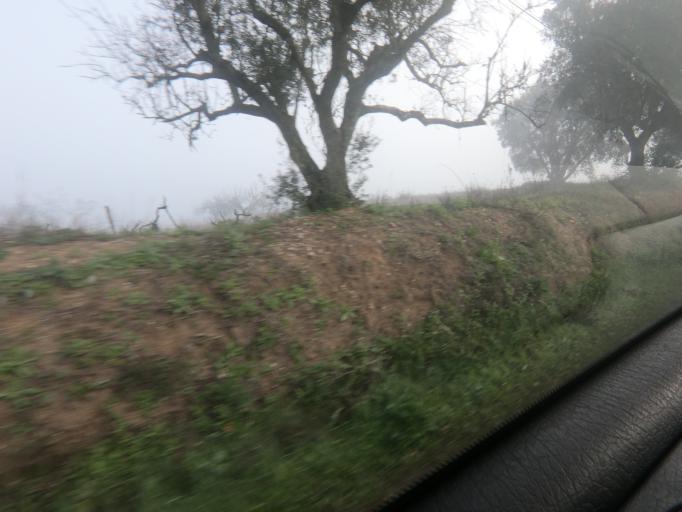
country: PT
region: Setubal
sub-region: Palmela
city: Pinhal Novo
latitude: 38.6089
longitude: -8.8637
